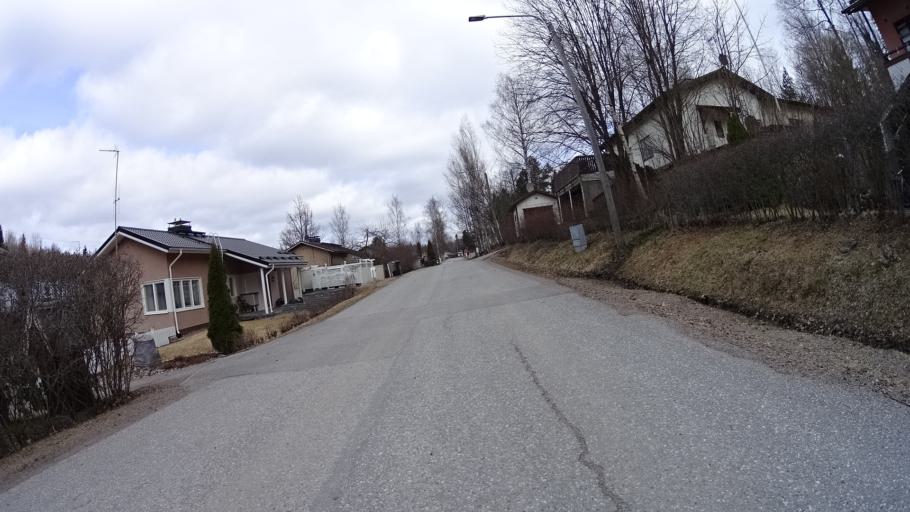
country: FI
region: Uusimaa
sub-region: Helsinki
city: Kilo
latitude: 60.2456
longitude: 24.7986
